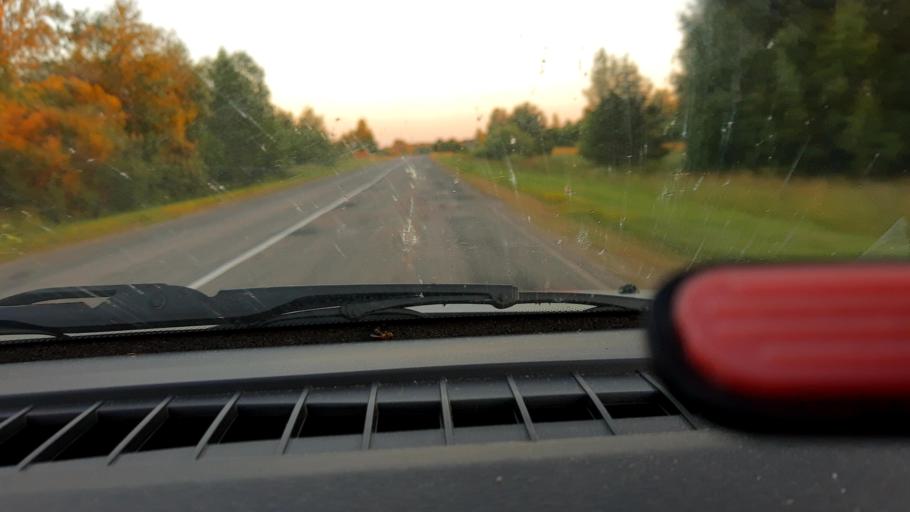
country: RU
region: Nizjnij Novgorod
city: Tonkino
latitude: 57.3184
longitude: 46.4715
